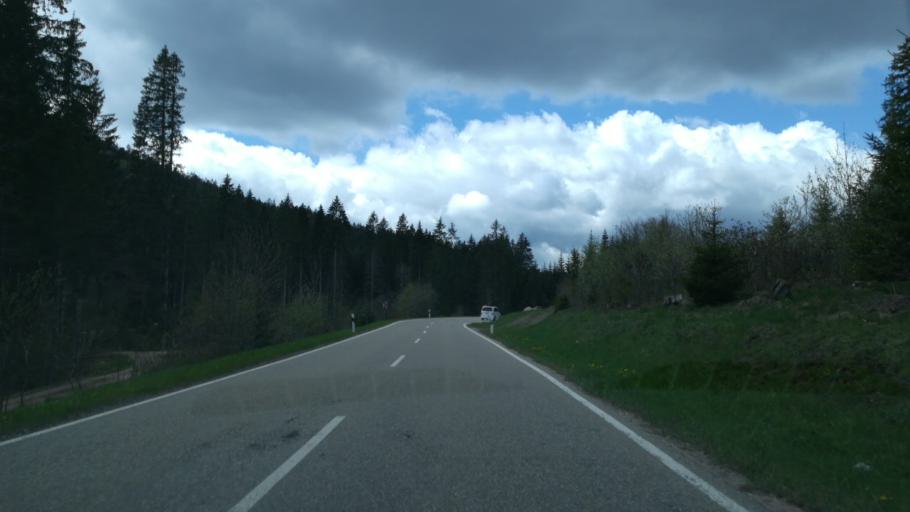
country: DE
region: Baden-Wuerttemberg
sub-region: Freiburg Region
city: Staufen
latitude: 47.7953
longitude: 8.2165
